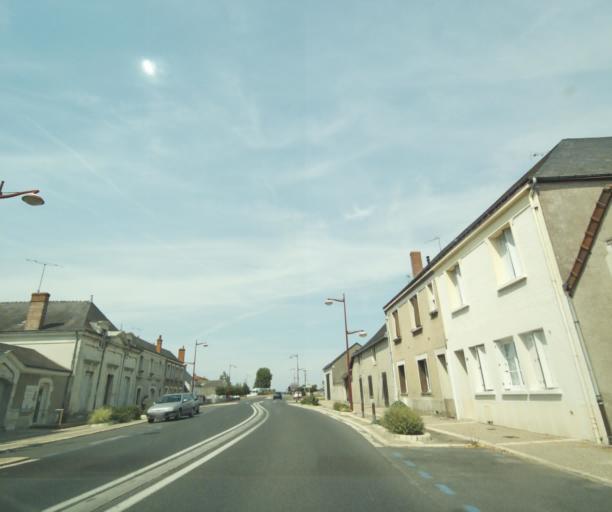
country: FR
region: Centre
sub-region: Departement d'Indre-et-Loire
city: La Celle-Saint-Avant
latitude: 47.0231
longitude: 0.6045
